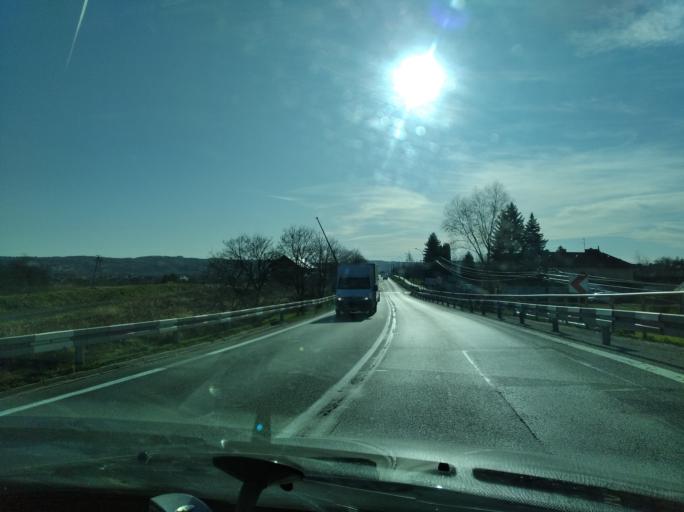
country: PL
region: Subcarpathian Voivodeship
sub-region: Powiat rzeszowski
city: Lutoryz
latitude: 49.9716
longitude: 21.9213
